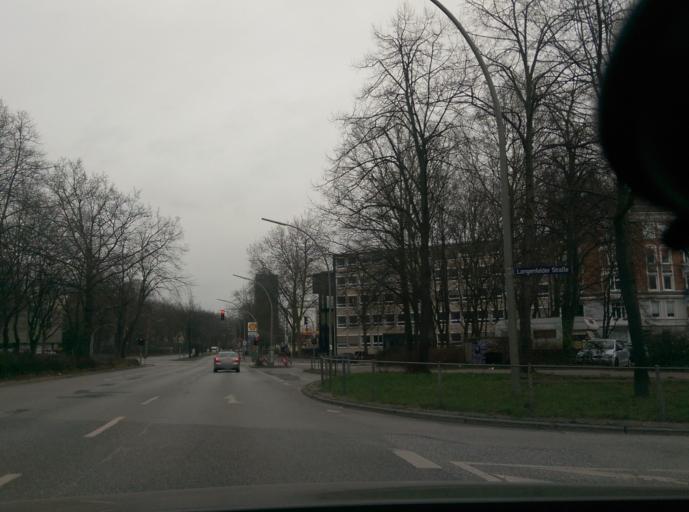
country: DE
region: Hamburg
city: St. Pauli
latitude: 53.5661
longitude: 9.9515
